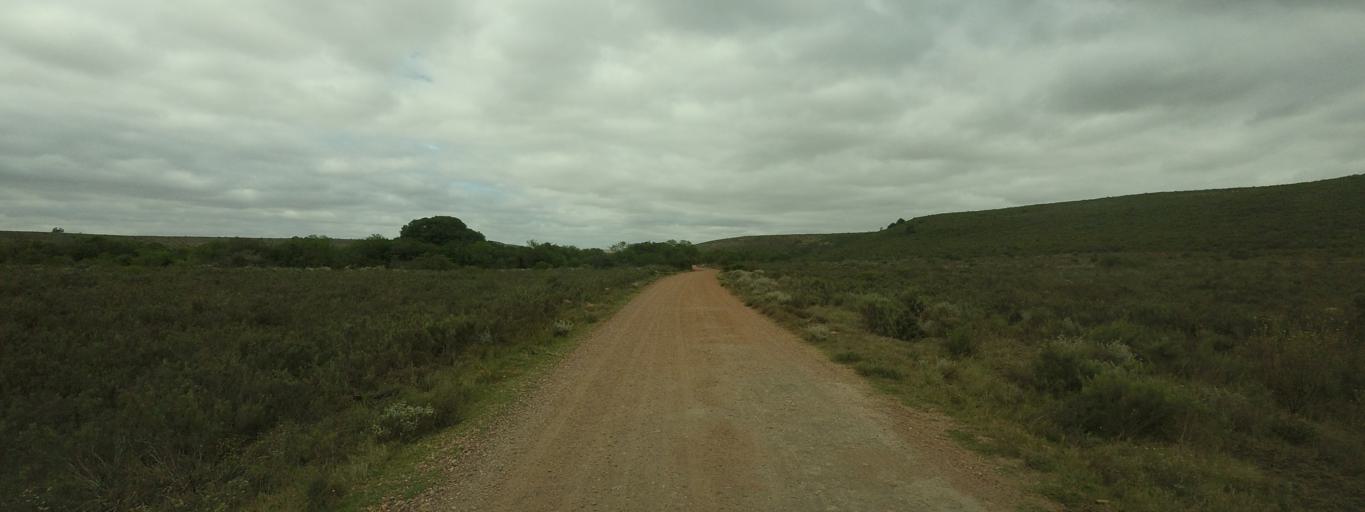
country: ZA
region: Western Cape
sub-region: Overberg District Municipality
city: Swellendam
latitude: -34.0649
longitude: 20.4385
